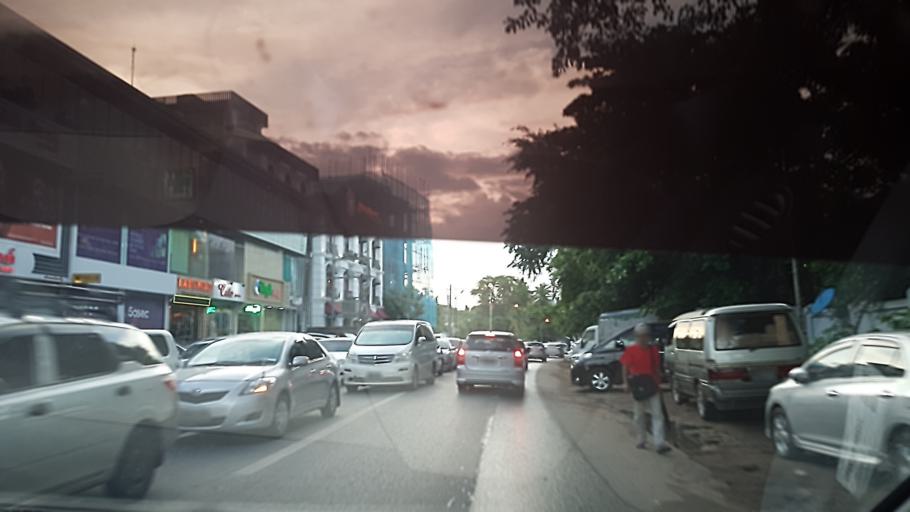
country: MM
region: Yangon
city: Yangon
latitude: 16.8067
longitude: 96.1451
